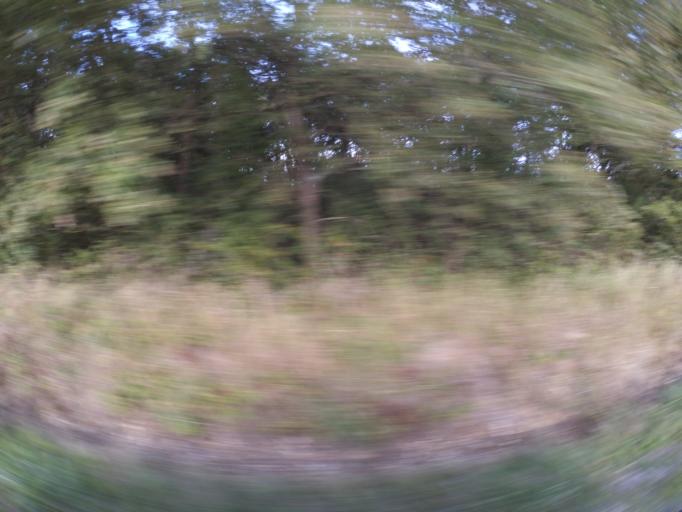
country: FR
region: Centre
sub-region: Departement d'Indre-et-Loire
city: Nazelles-Negron
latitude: 47.4562
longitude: 0.9360
